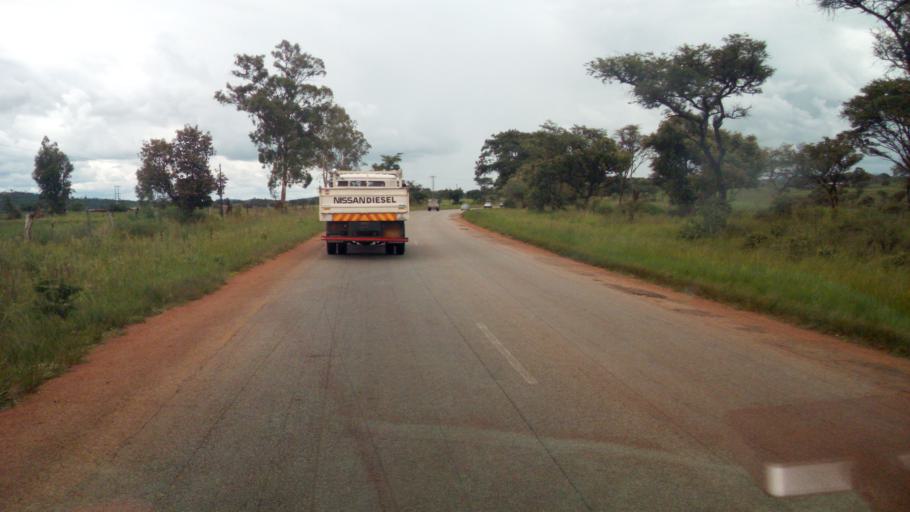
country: ZW
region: Mashonaland Central
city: Mazowe
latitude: -17.6500
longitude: 30.9839
